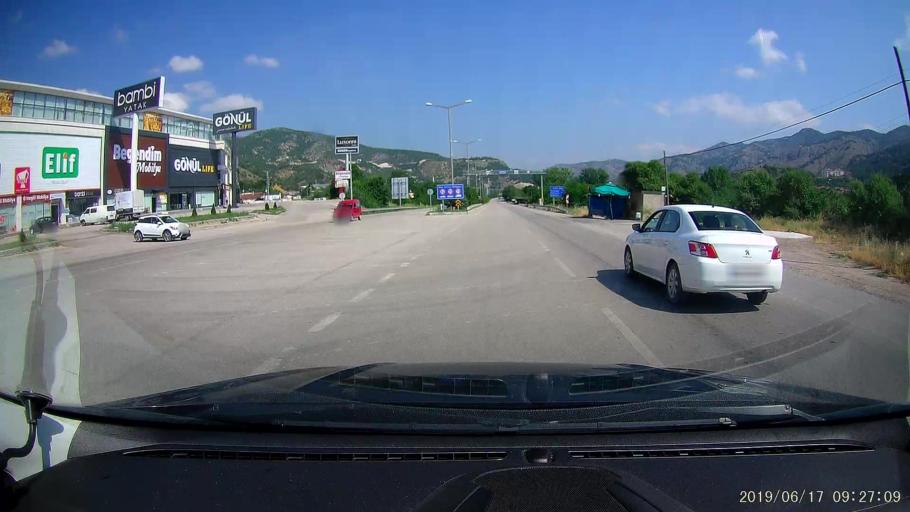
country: TR
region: Amasya
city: Amasya
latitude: 40.6743
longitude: 35.8287
